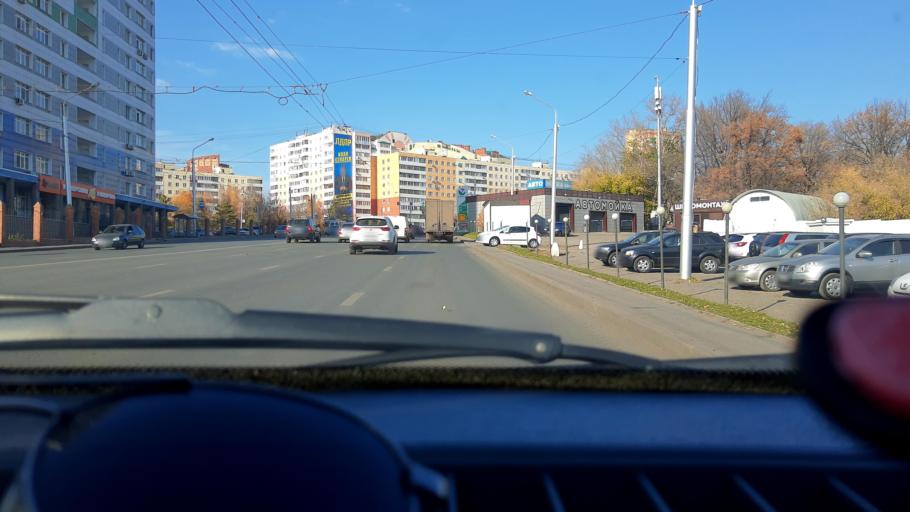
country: RU
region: Bashkortostan
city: Ufa
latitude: 54.7605
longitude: 56.0236
